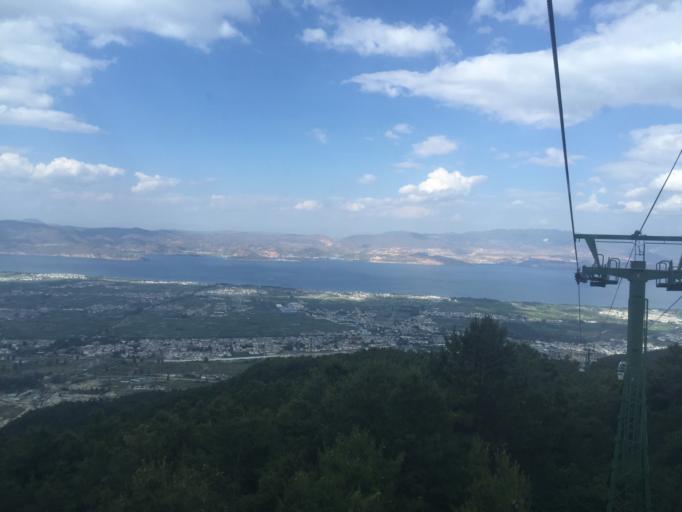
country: CN
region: Yunnan
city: Dali
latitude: 25.6477
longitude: 100.1564
